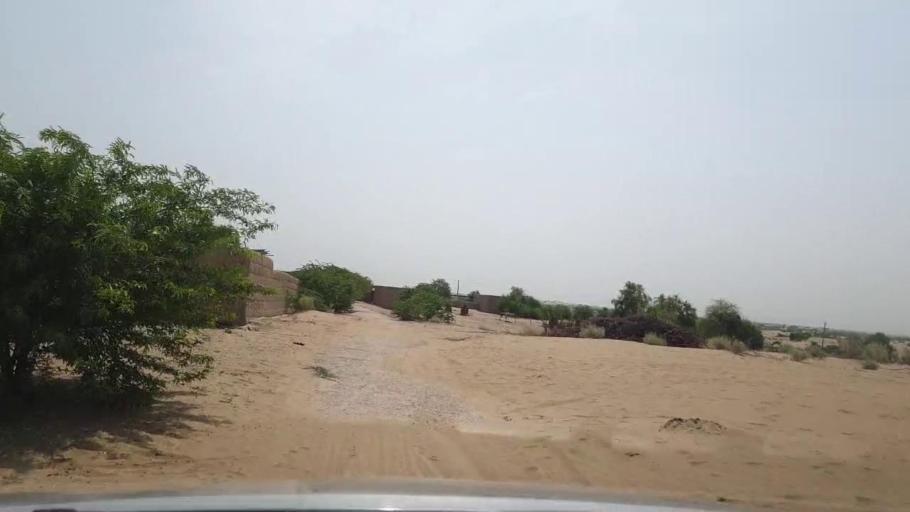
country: PK
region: Sindh
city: Pano Aqil
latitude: 27.6081
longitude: 69.1539
